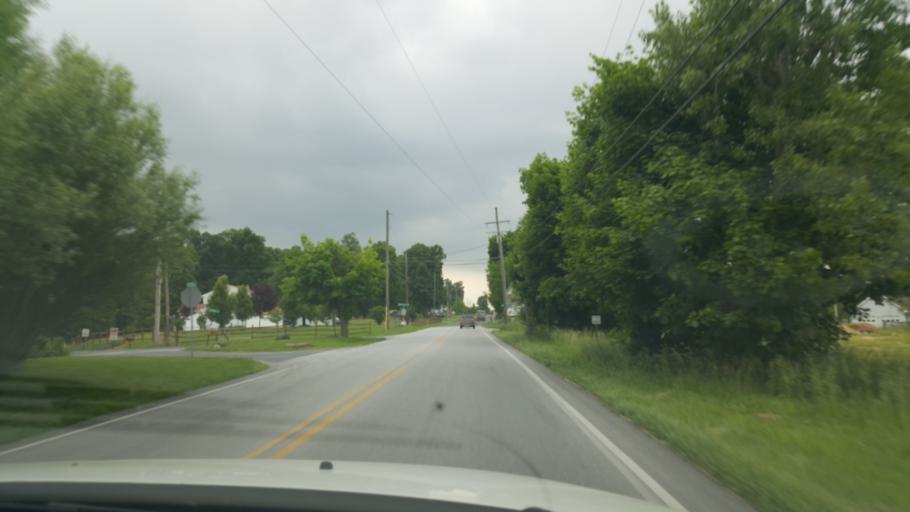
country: US
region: Pennsylvania
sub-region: Adams County
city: Lake Meade
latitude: 39.9483
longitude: -77.1011
